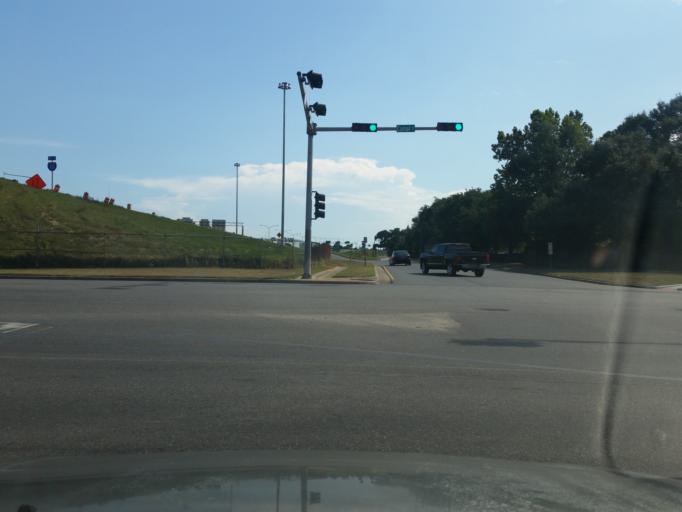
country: US
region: Alabama
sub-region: Mobile County
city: Mobile
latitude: 30.6835
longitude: -88.0432
